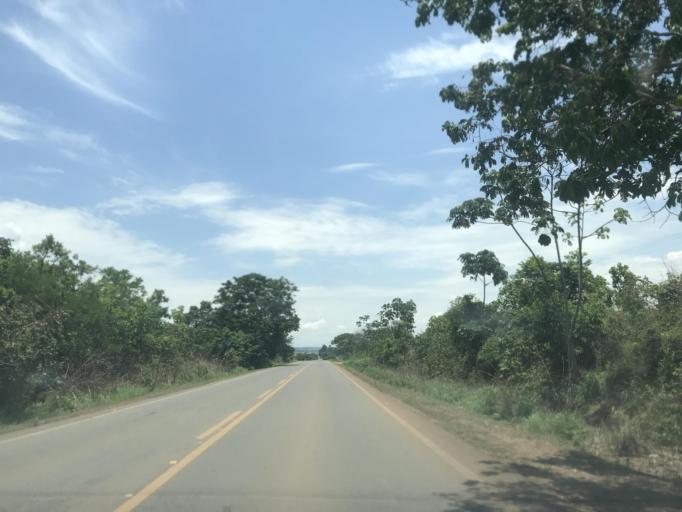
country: BR
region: Goias
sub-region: Vianopolis
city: Vianopolis
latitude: -16.6202
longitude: -48.3531
